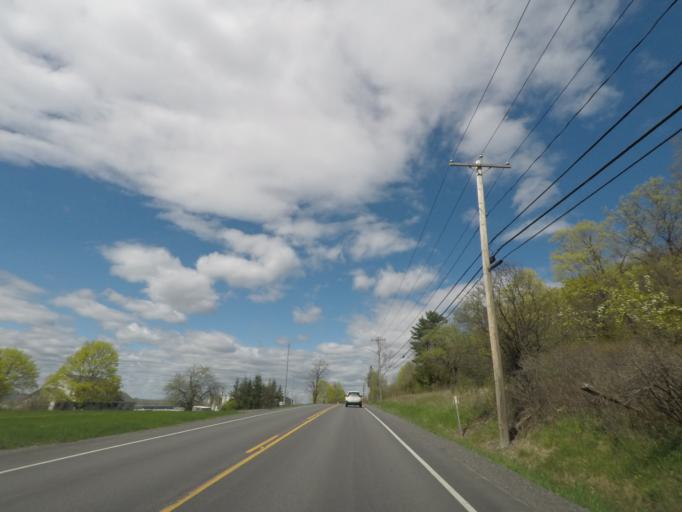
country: US
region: New York
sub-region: Columbia County
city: Oakdale
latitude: 42.2254
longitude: -73.7861
